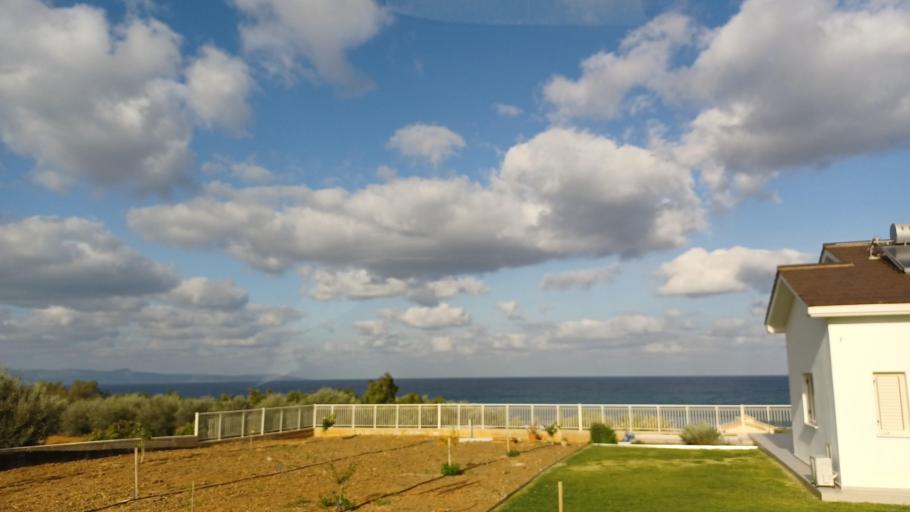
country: CY
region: Pafos
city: Polis
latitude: 35.1276
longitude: 32.5194
